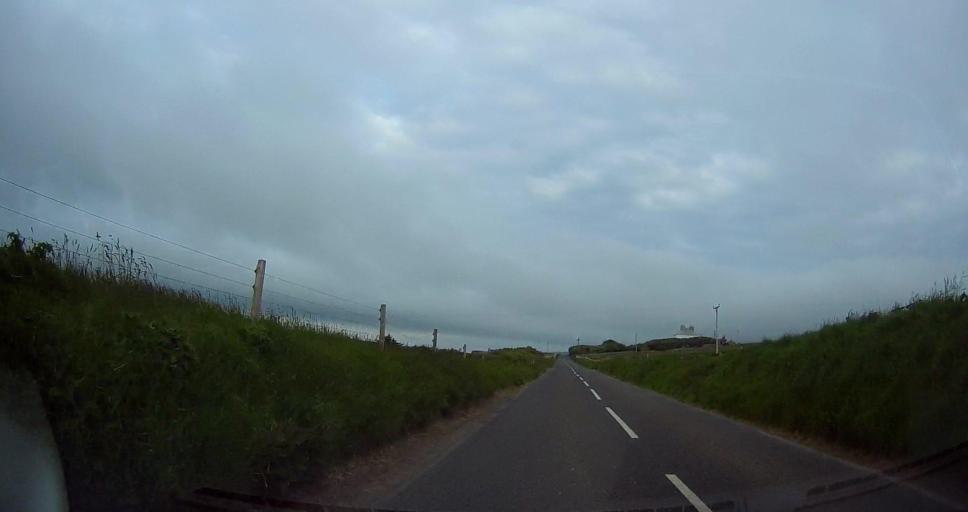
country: GB
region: Scotland
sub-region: Orkney Islands
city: Orkney
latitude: 59.1180
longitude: -3.1179
